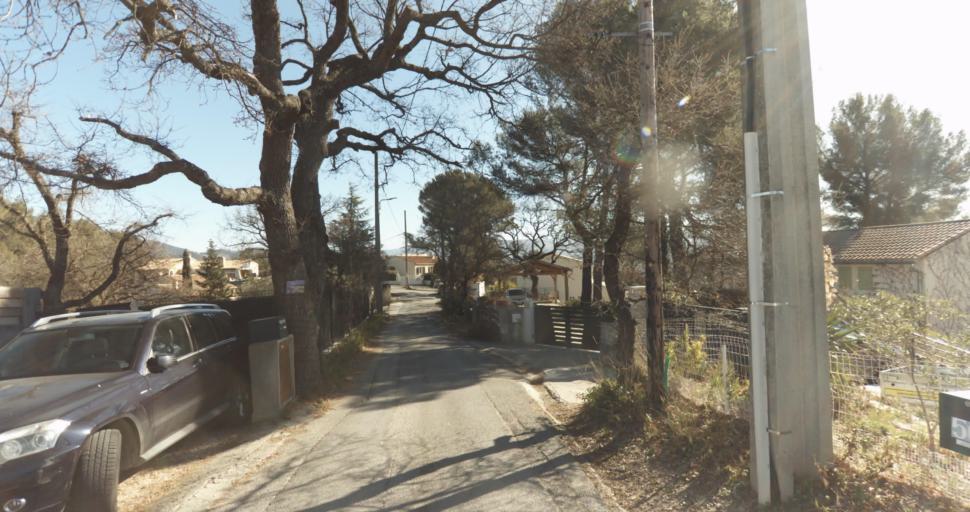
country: FR
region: Provence-Alpes-Cote d'Azur
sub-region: Departement des Bouches-du-Rhone
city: La Bouilladisse
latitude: 43.3877
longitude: 5.5904
